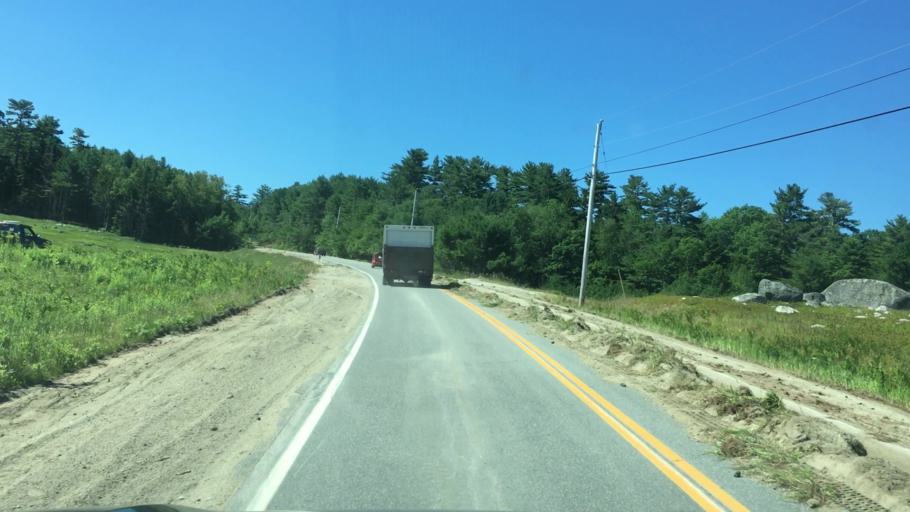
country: US
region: Maine
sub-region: Hancock County
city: Sedgwick
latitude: 44.3527
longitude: -68.5865
